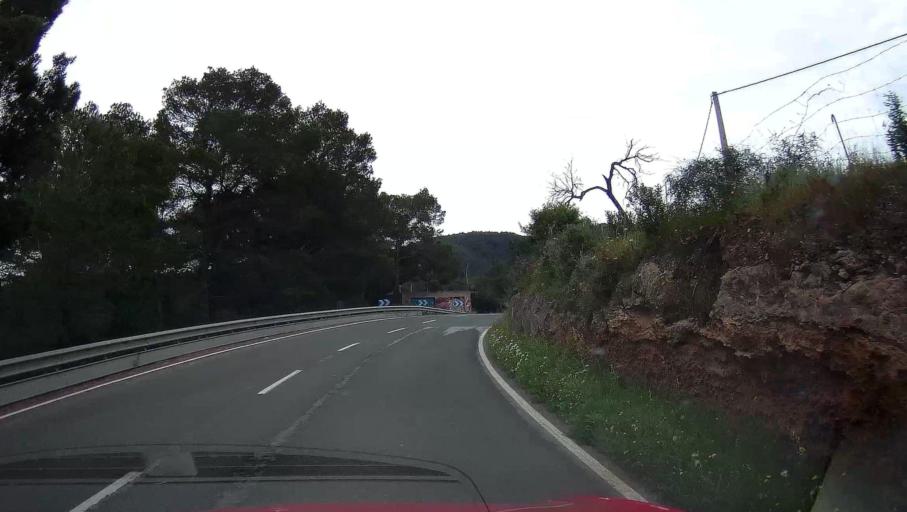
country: ES
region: Balearic Islands
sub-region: Illes Balears
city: Sant Joan de Labritja
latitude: 39.0910
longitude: 1.5023
